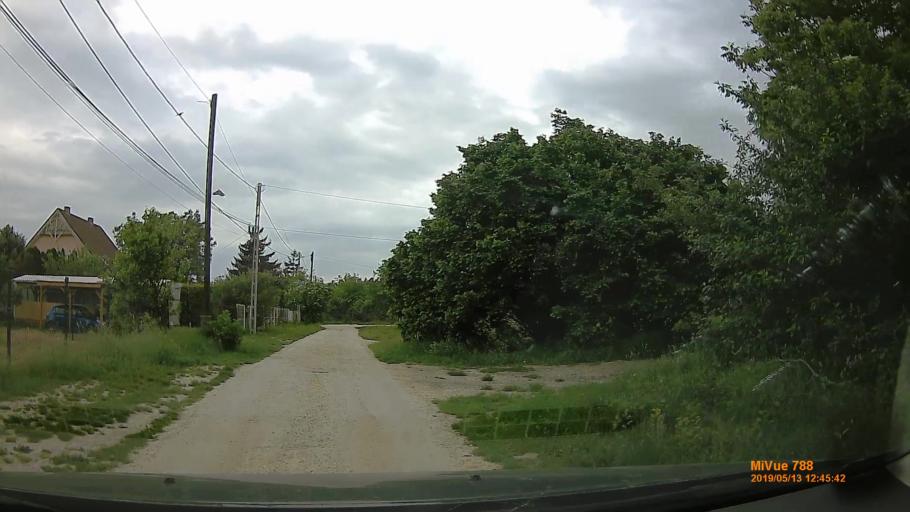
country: HU
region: Pest
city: Diosd
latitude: 47.4031
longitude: 18.9872
